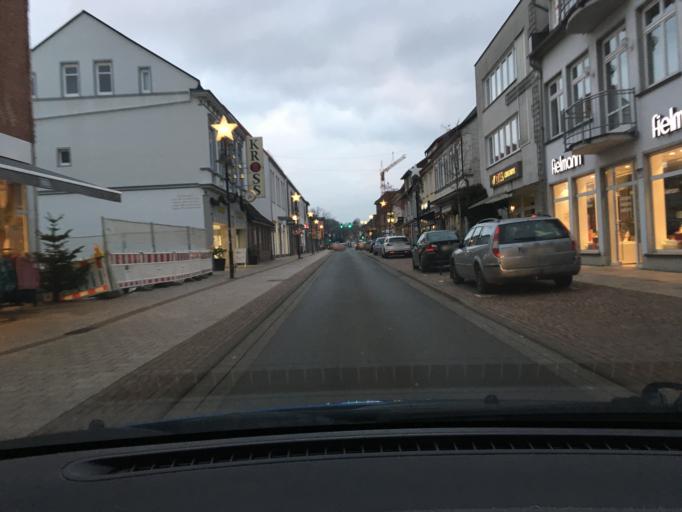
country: DE
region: Lower Saxony
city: Walsrode
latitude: 52.8625
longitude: 9.5897
